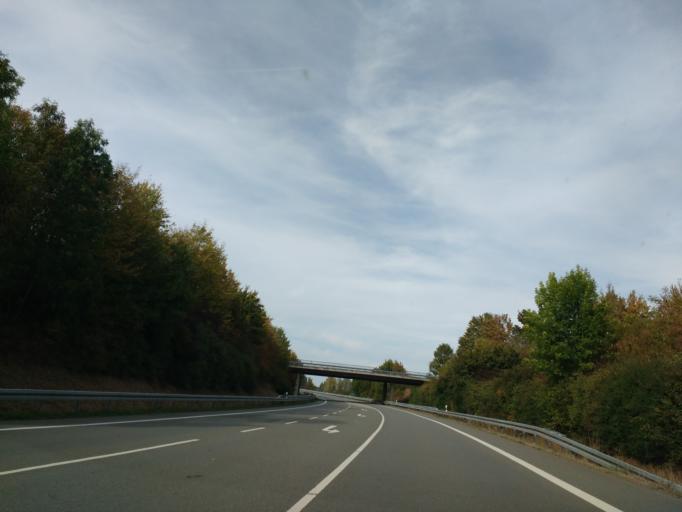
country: DE
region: North Rhine-Westphalia
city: Borgentreich
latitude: 51.5977
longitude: 9.1398
